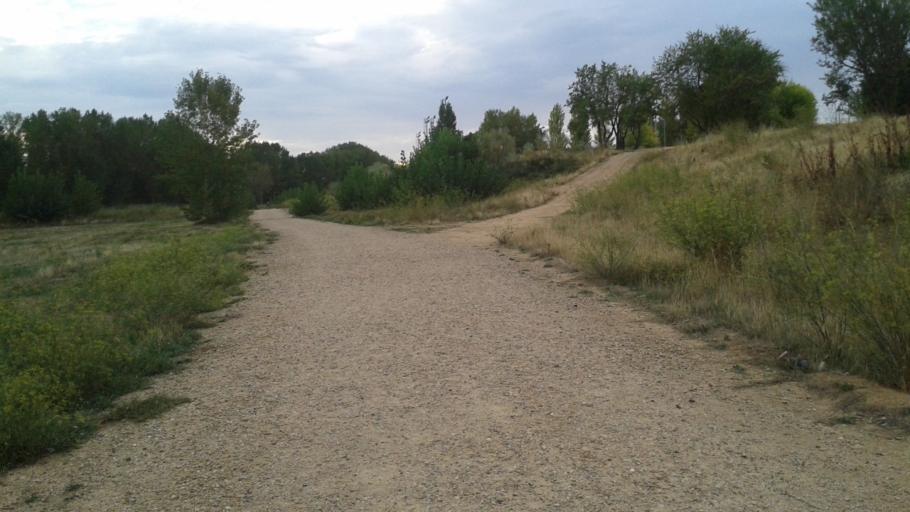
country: ES
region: Castille and Leon
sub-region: Provincia de Valladolid
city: Arroyo
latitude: 41.6122
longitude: -4.7796
